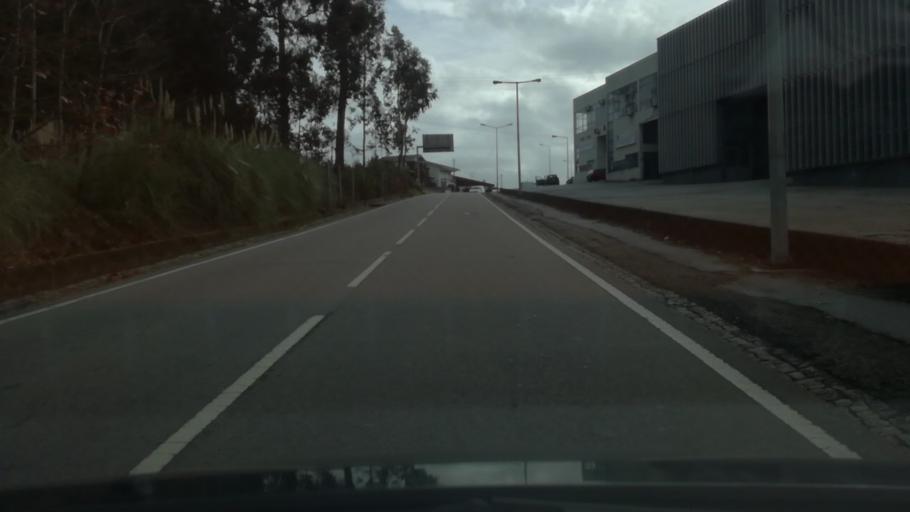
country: PT
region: Porto
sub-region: Maia
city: Maia
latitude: 41.2430
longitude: -8.6351
